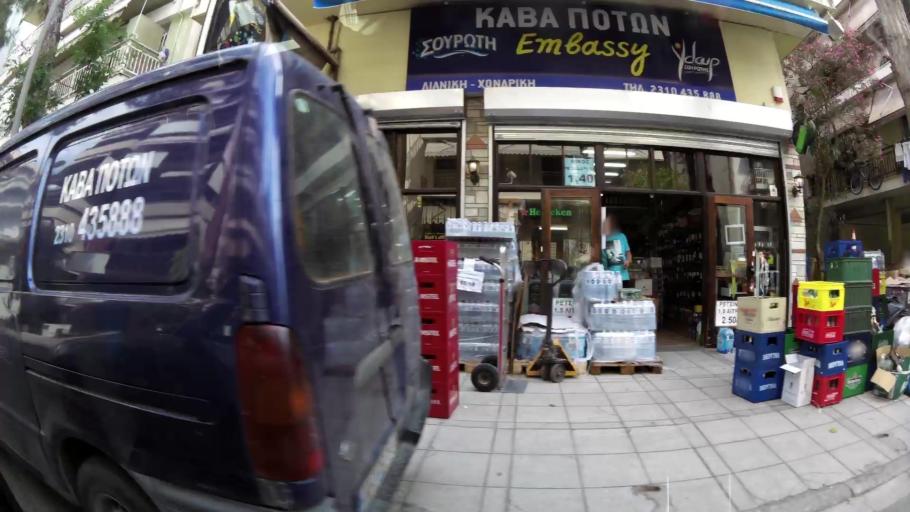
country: GR
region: Central Macedonia
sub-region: Nomos Thessalonikis
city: Kalamaria
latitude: 40.5752
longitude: 22.9512
